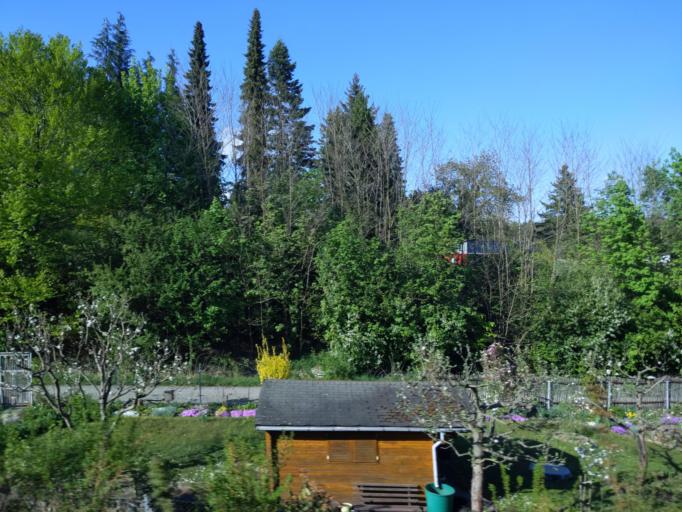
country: DE
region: Saxony
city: Radeberg
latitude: 51.1150
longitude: 13.8961
